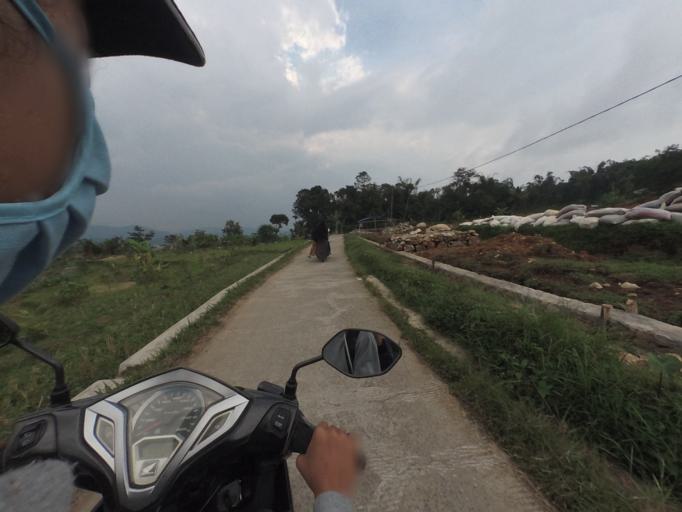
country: ID
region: West Java
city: Ciampea
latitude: -6.6880
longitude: 106.6529
